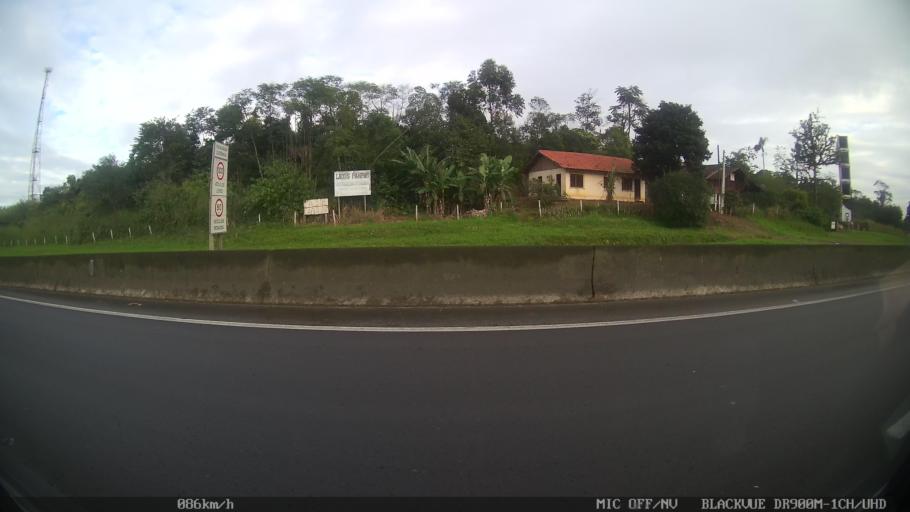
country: BR
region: Santa Catarina
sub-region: Barra Velha
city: Barra Velha
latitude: -26.5780
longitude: -48.7224
